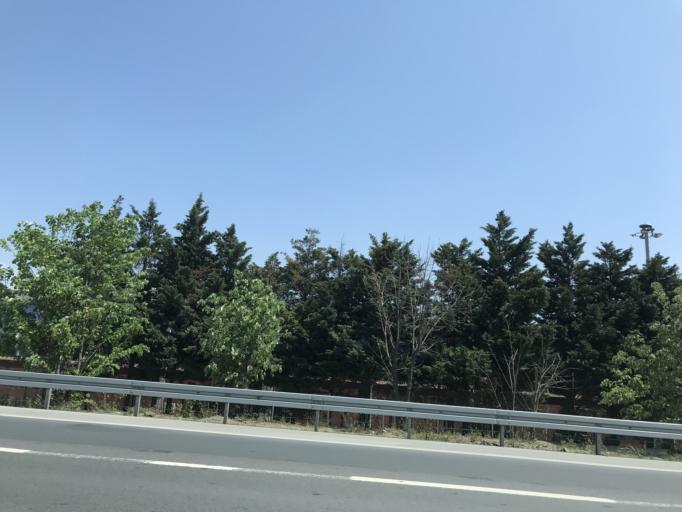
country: TR
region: Istanbul
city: Sisli
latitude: 41.0841
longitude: 28.9613
